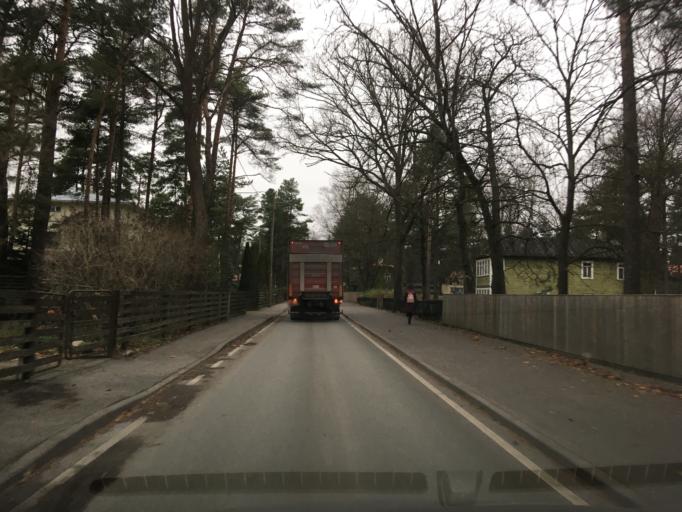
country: EE
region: Harju
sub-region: Saue vald
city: Laagri
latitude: 59.3809
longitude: 24.6742
